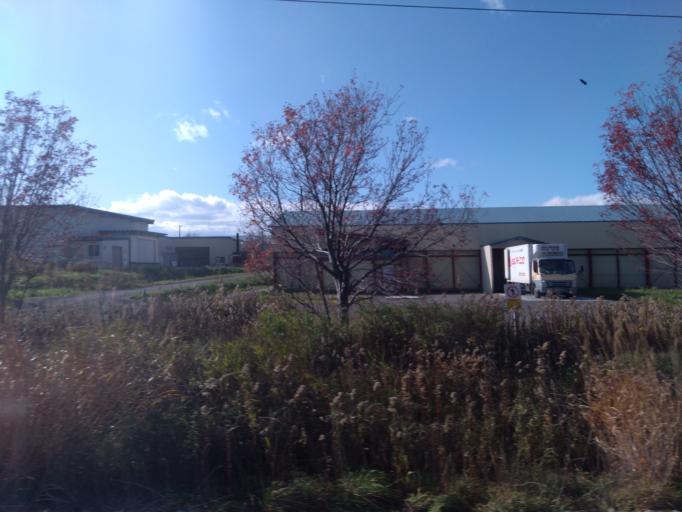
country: JP
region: Hokkaido
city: Kitahiroshima
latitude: 42.9564
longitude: 141.5697
